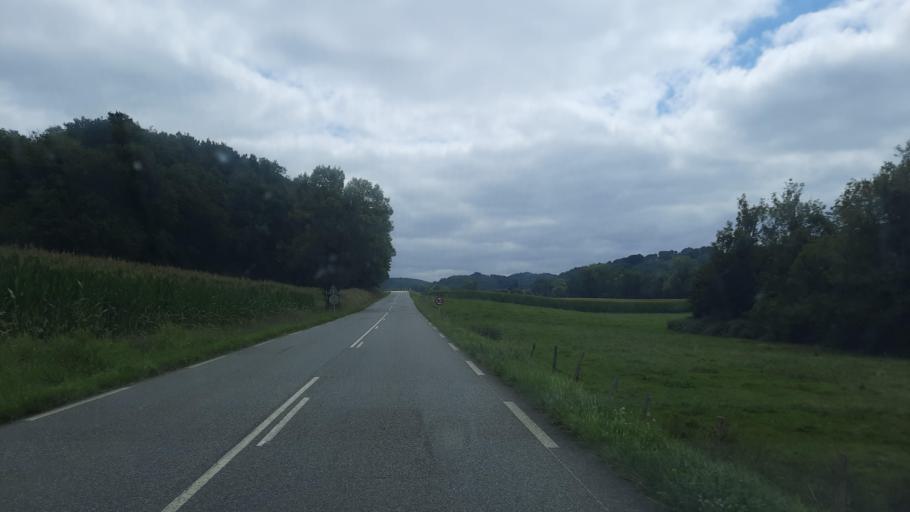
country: FR
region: Midi-Pyrenees
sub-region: Departement des Hautes-Pyrenees
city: Trie-sur-Baise
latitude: 43.3042
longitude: 0.2698
